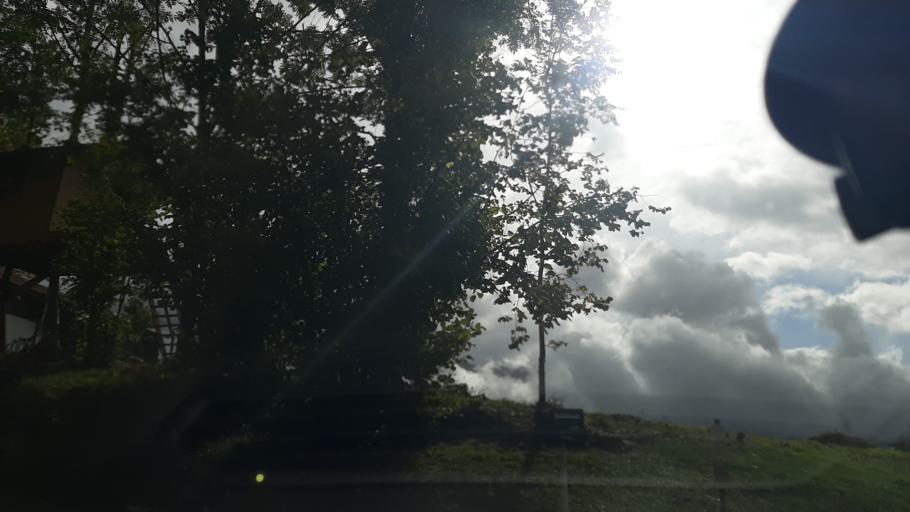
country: FR
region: Rhone-Alpes
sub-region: Departement de la Savoie
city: Gresy-sur-Isere
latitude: 45.6067
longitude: 6.2703
